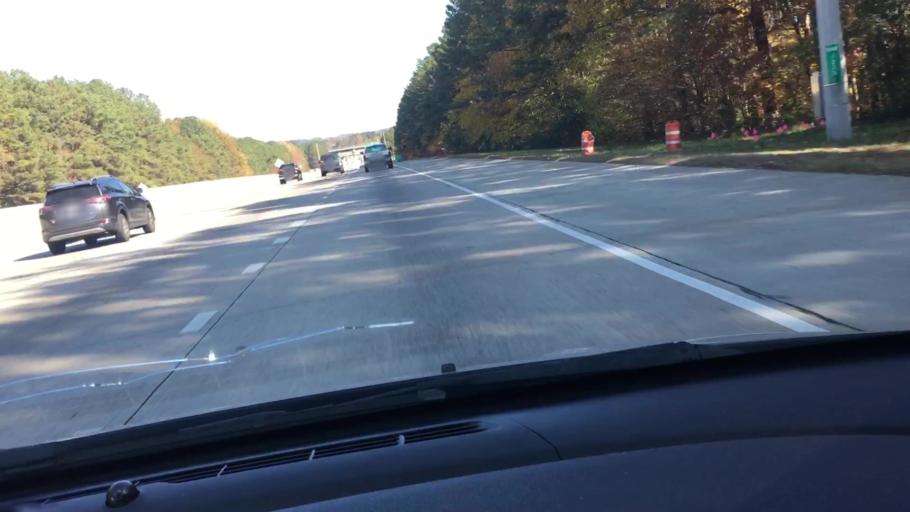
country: US
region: Georgia
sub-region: Fulton County
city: Alpharetta
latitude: 34.1100
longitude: -84.2326
